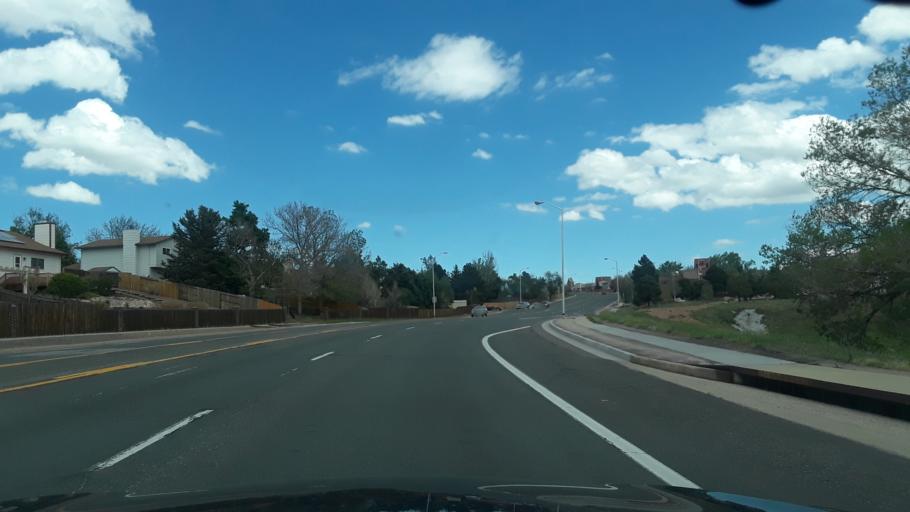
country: US
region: Colorado
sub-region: El Paso County
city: Air Force Academy
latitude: 38.9440
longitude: -104.7830
